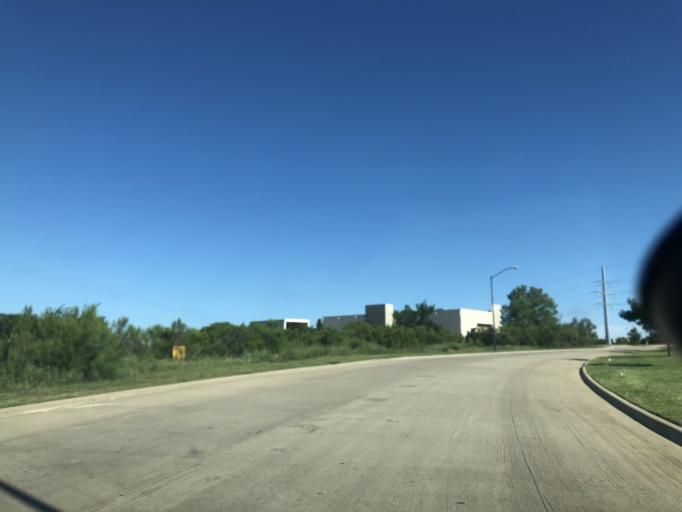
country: US
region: Texas
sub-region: Tarrant County
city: Euless
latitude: 32.8104
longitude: -97.0425
